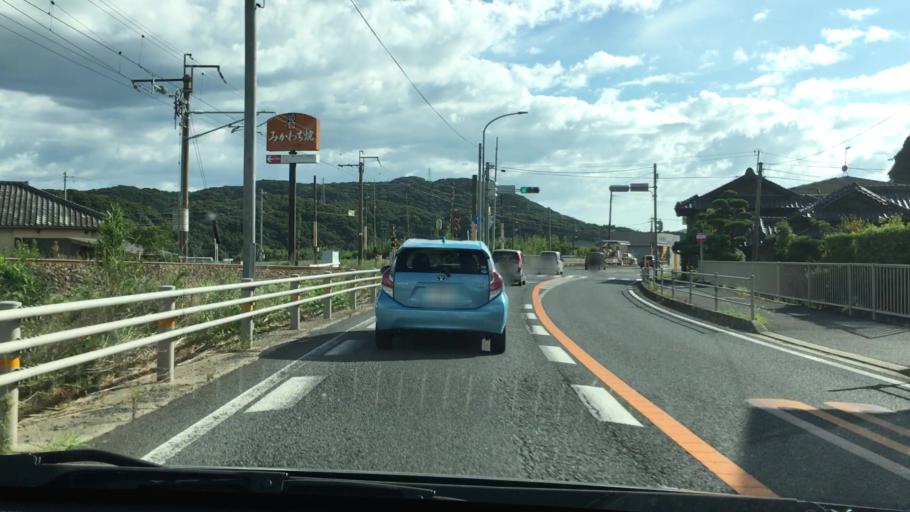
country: JP
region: Nagasaki
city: Sasebo
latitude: 33.1463
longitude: 129.8274
